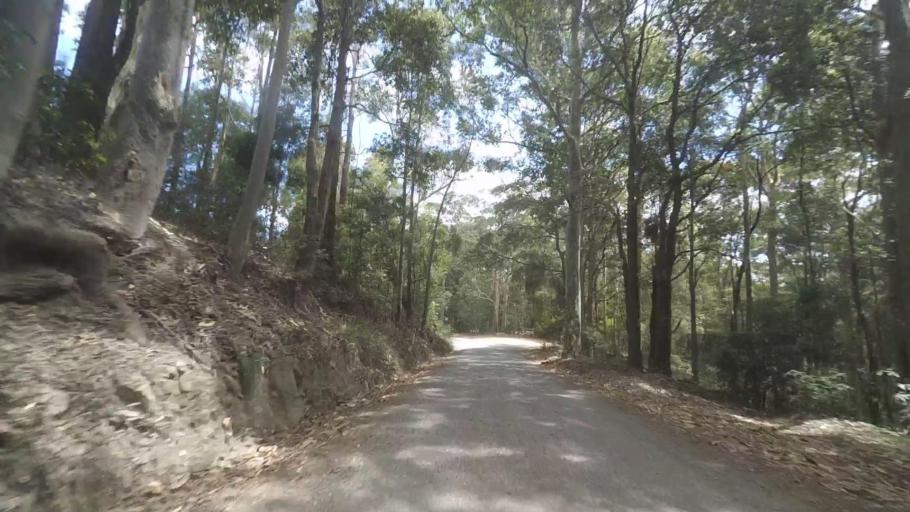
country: AU
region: New South Wales
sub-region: Shoalhaven Shire
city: Milton
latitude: -35.4356
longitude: 150.3314
